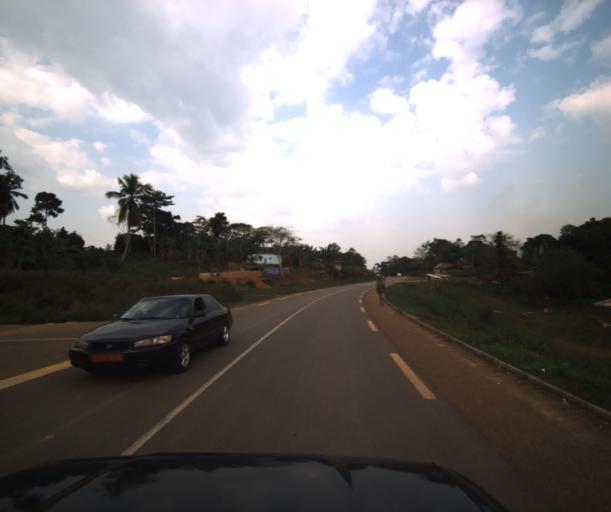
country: CM
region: Centre
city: Akono
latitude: 3.6057
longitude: 11.3110
